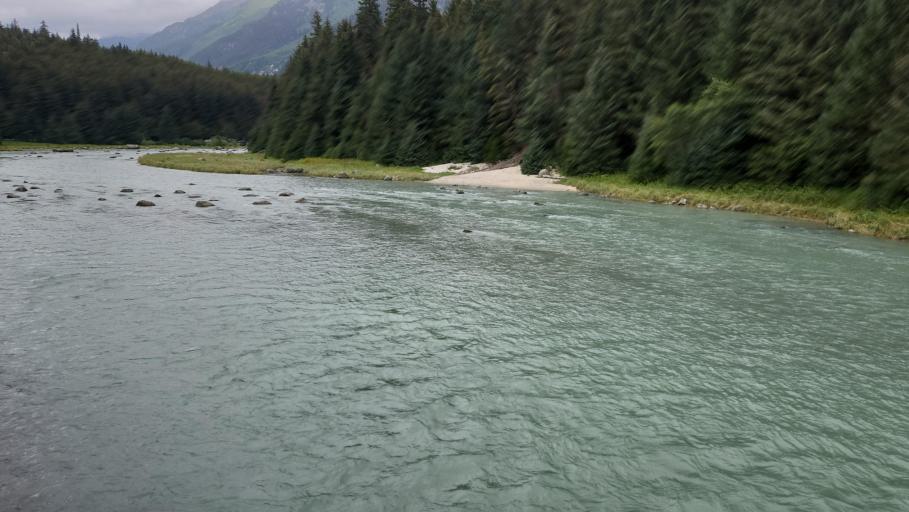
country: US
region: Alaska
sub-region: Haines Borough
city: Haines
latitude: 59.3244
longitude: -135.5579
